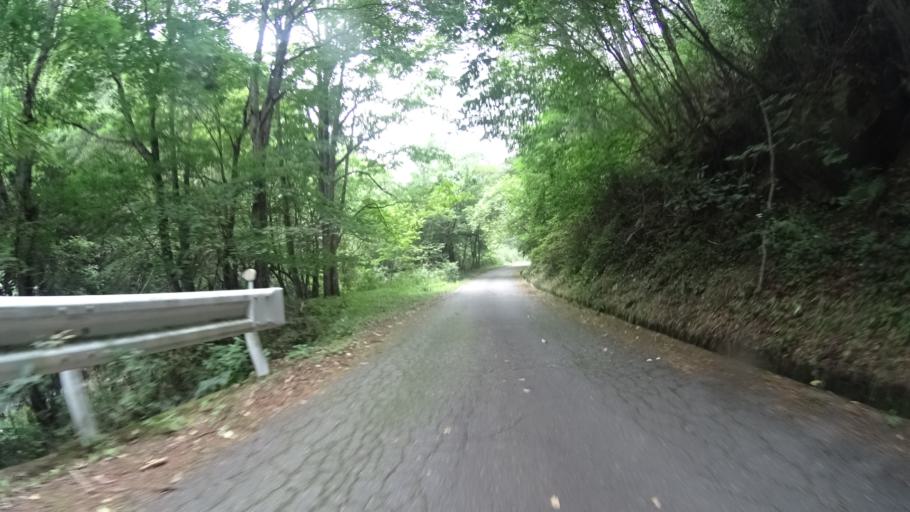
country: JP
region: Yamanashi
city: Kofu-shi
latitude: 35.8165
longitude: 138.5980
